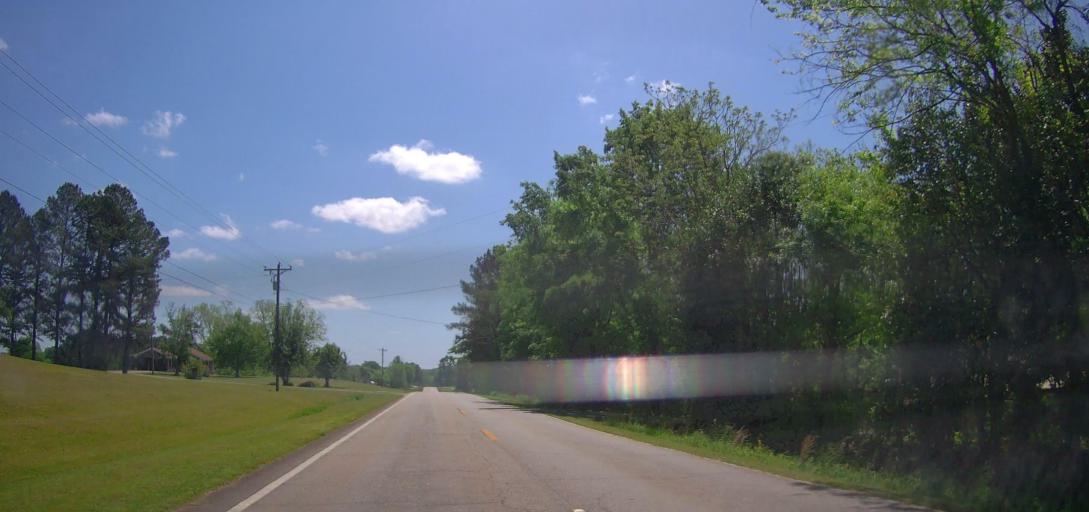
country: US
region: Georgia
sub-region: Jones County
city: Gray
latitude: 33.0381
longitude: -83.5876
